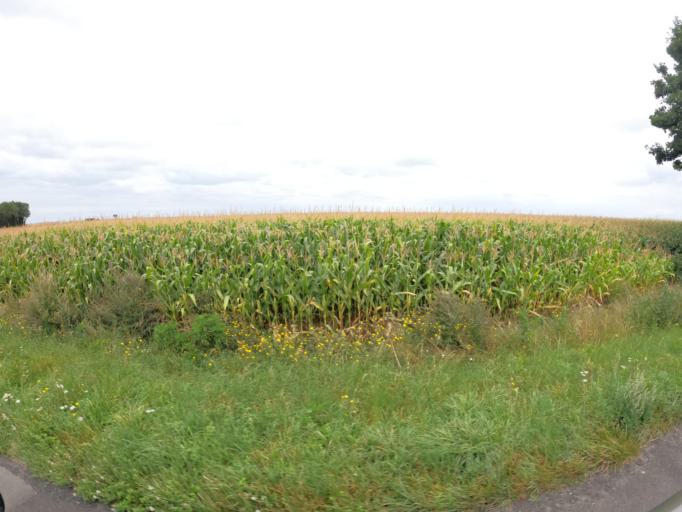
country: FR
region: Pays de la Loire
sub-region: Departement de la Vendee
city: Sainte-Hermine
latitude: 46.5324
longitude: -1.0095
